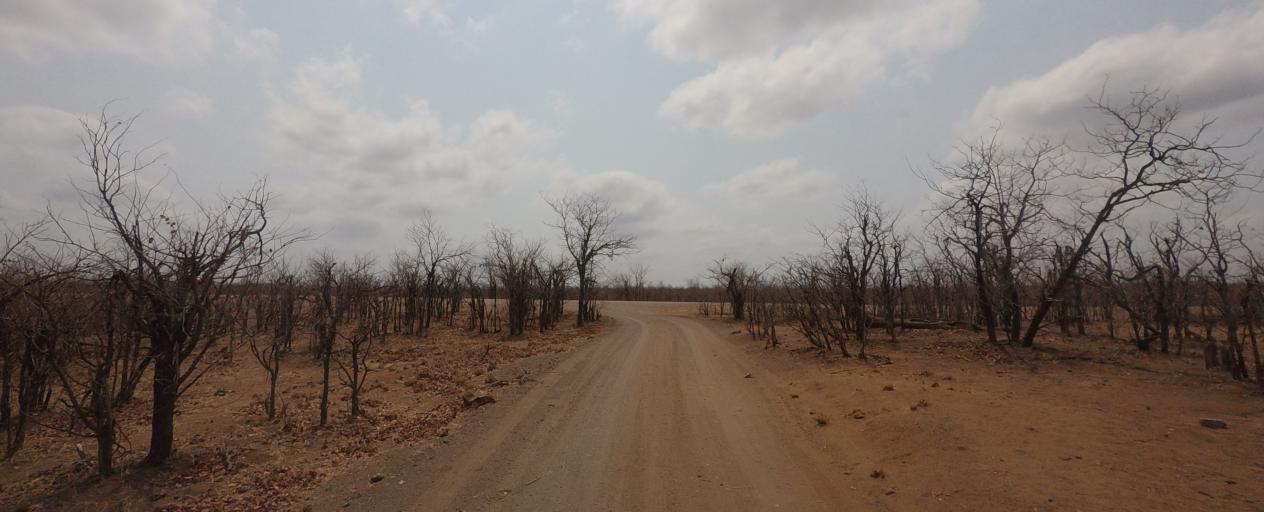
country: ZA
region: Limpopo
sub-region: Mopani District Municipality
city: Phalaborwa
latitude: -23.5398
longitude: 31.4236
